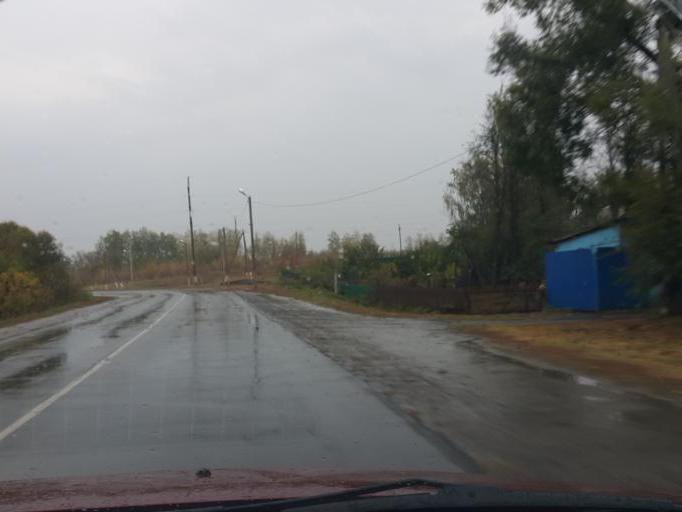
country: RU
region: Tambov
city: Znamenka
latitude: 52.4067
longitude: 41.4595
